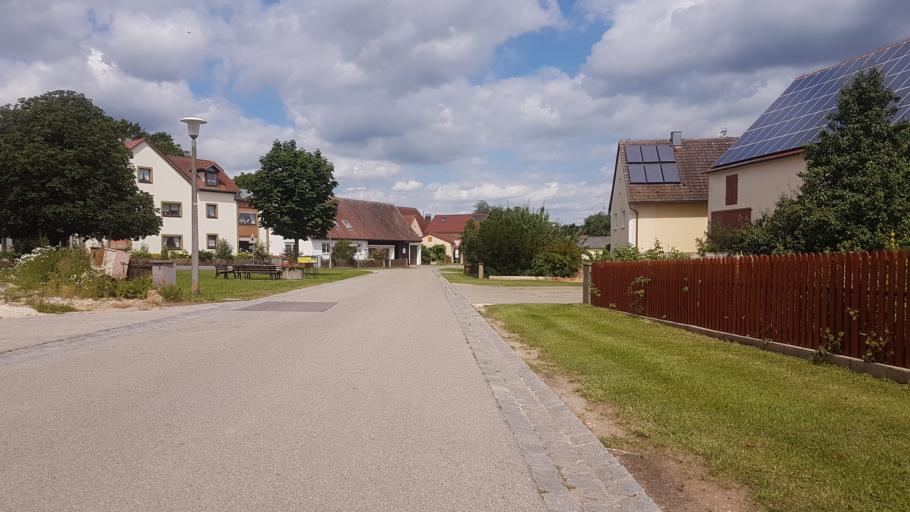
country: DE
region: Bavaria
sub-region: Regierungsbezirk Mittelfranken
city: Gunzenhausen
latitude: 49.0942
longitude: 10.7532
